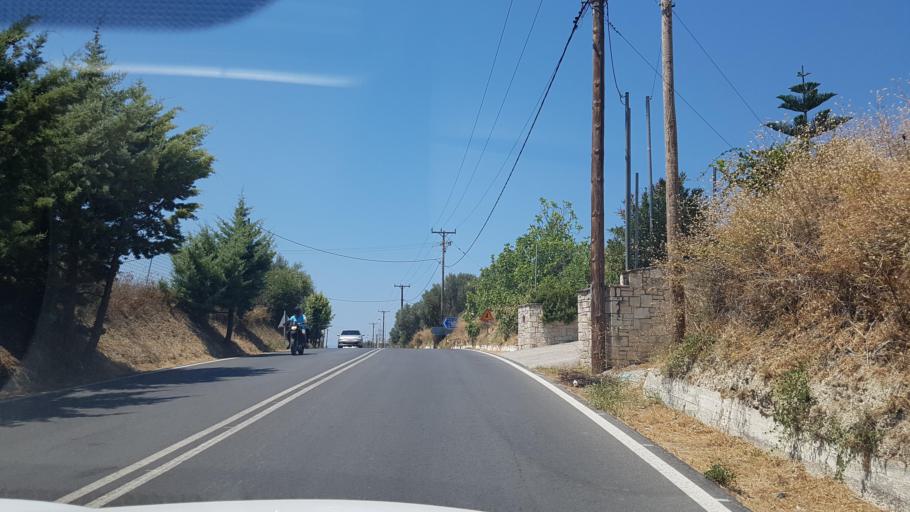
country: GR
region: Crete
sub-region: Nomos Rethymnis
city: Rethymno
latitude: 35.3574
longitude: 24.5553
